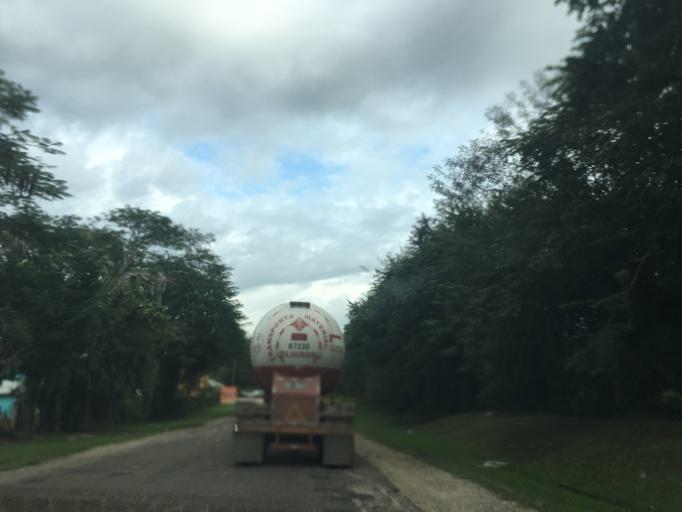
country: BZ
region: Cayo
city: San Ignacio
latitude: 17.2035
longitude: -88.9550
